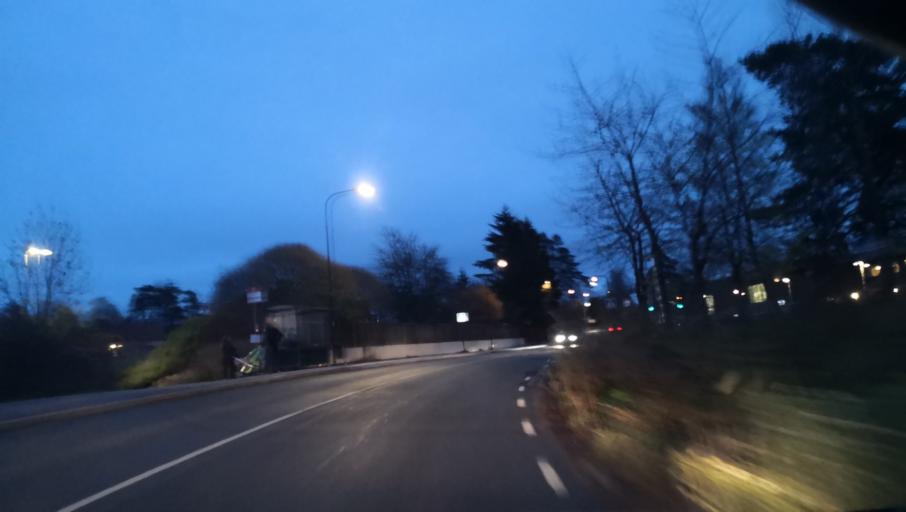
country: SE
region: Stockholm
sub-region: Taby Kommun
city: Taby
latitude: 59.4458
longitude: 18.1085
